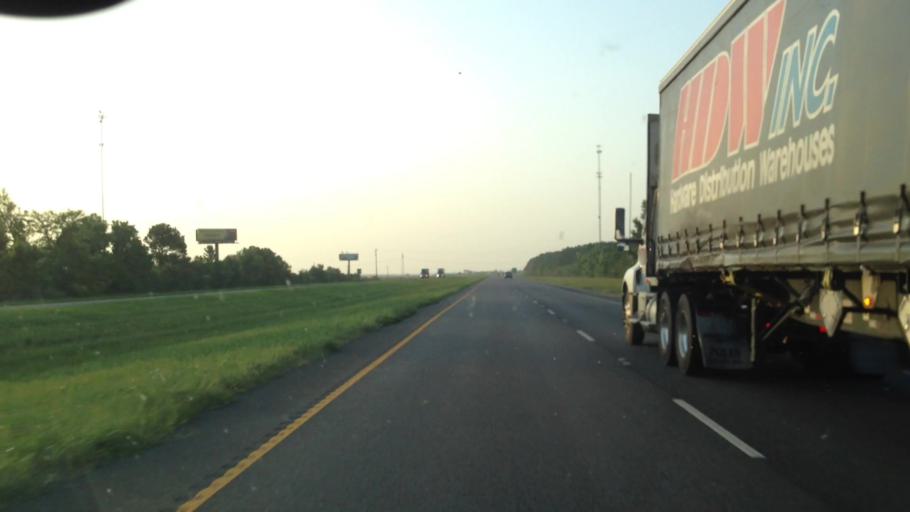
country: US
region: Louisiana
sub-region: Red River Parish
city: Coushatta
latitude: 31.8454
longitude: -93.2923
